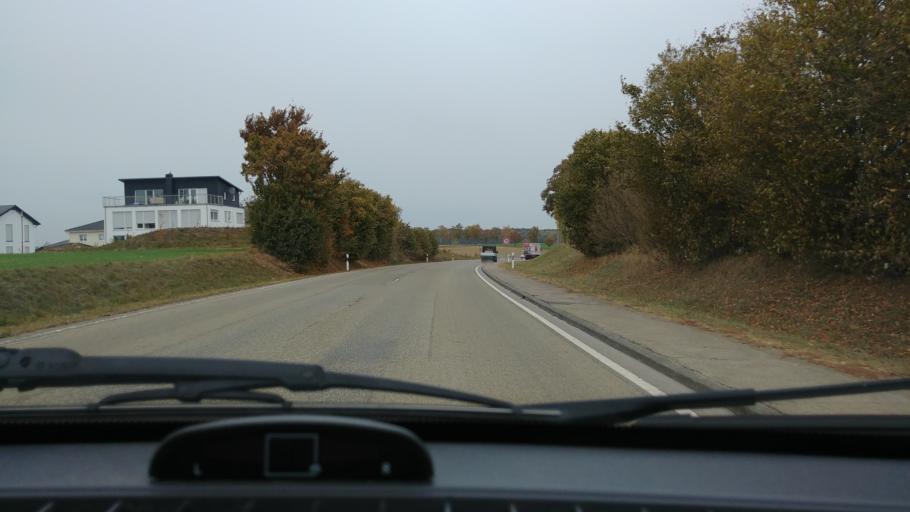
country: DE
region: Baden-Wuerttemberg
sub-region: Regierungsbezirk Stuttgart
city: Rot am See
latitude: 49.2512
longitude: 10.0366
